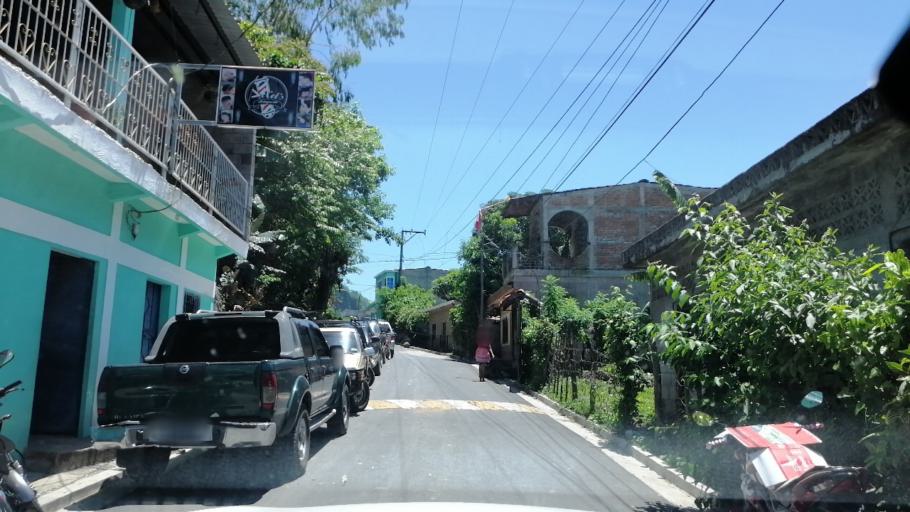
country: SV
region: San Miguel
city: Ciudad Barrios
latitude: 13.8322
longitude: -88.2270
